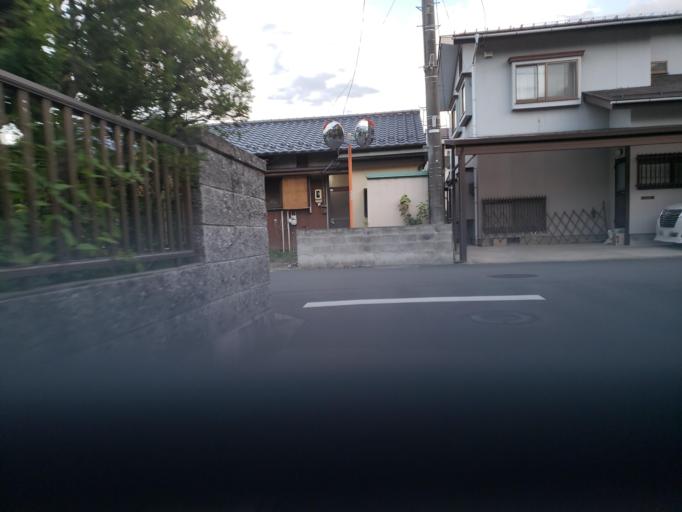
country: JP
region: Nagano
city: Nagano-shi
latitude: 36.6264
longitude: 138.1608
